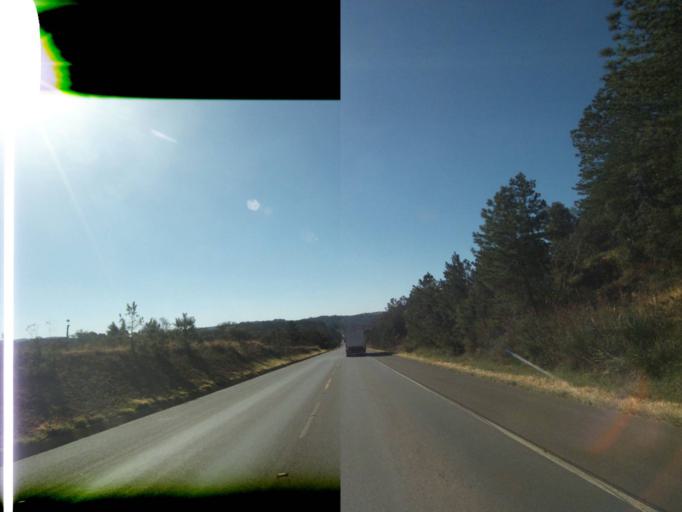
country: BR
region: Parana
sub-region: Tibagi
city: Tibagi
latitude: -24.5955
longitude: -50.4374
